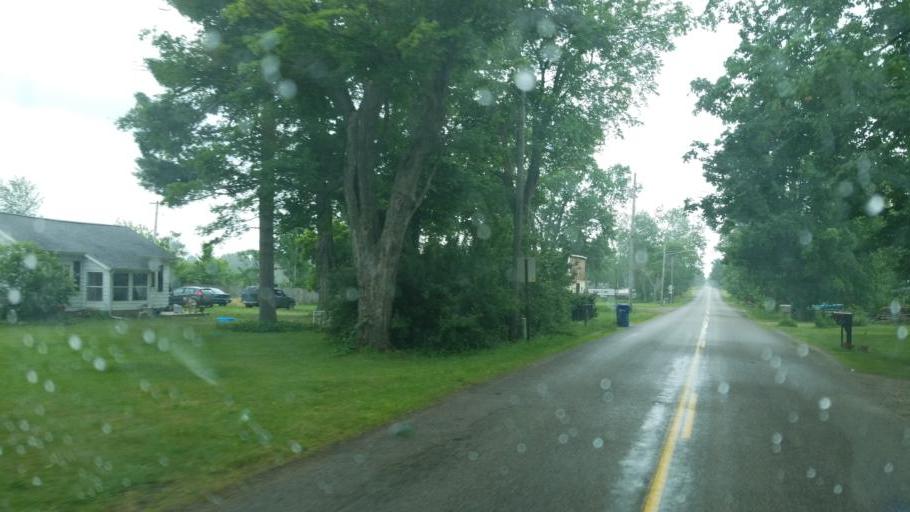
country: US
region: Michigan
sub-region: Barry County
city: Nashville
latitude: 42.5427
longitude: -85.0138
